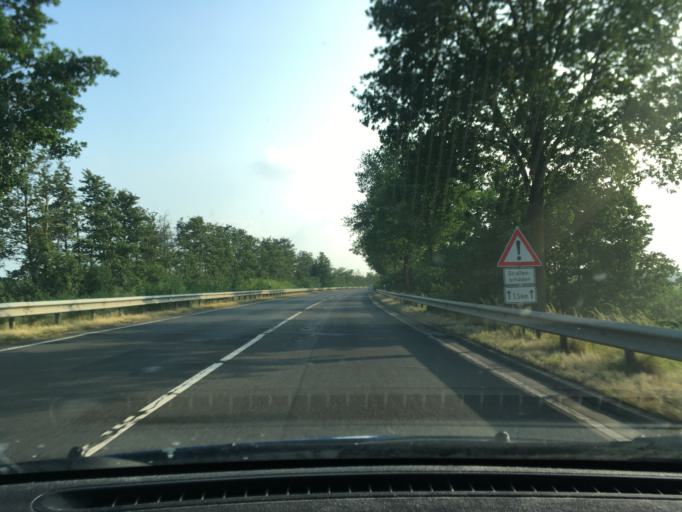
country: DE
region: Lower Saxony
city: Winsen
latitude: 53.3586
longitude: 10.1688
